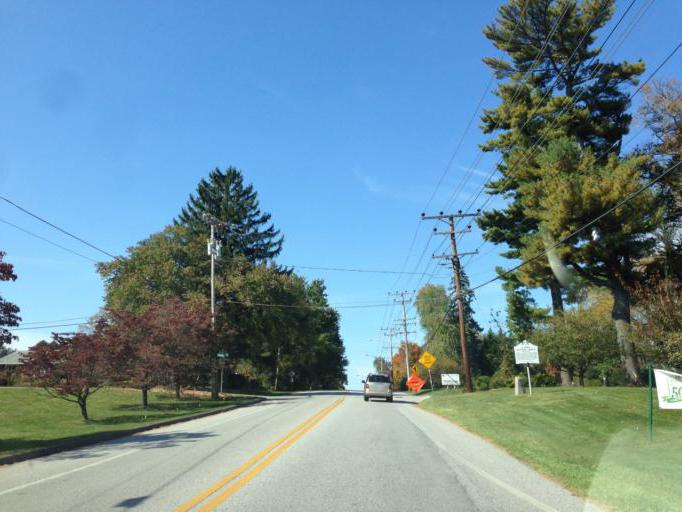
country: US
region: Maryland
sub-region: Howard County
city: Ellicott City
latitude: 39.2726
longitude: -76.8296
